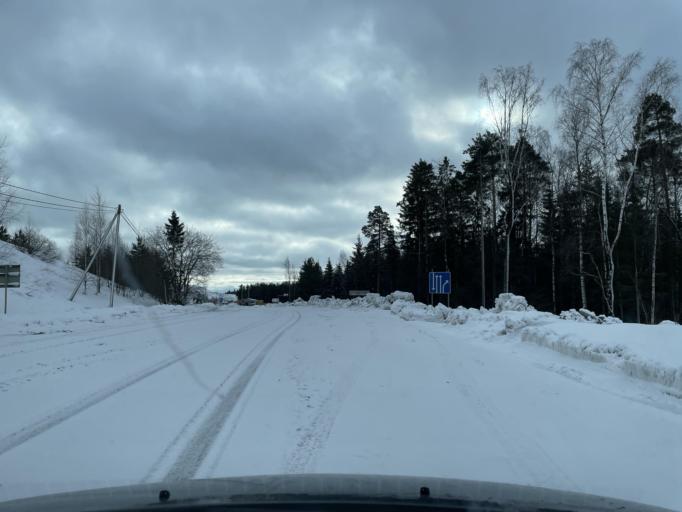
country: FI
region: Uusimaa
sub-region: Helsinki
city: Espoo
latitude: 60.2373
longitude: 24.5559
